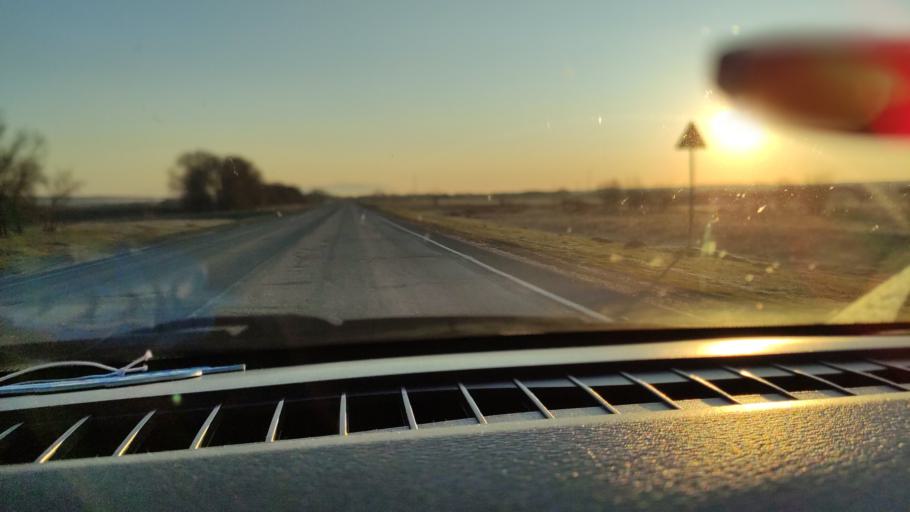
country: RU
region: Saratov
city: Sinodskoye
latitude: 51.9687
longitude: 46.6377
